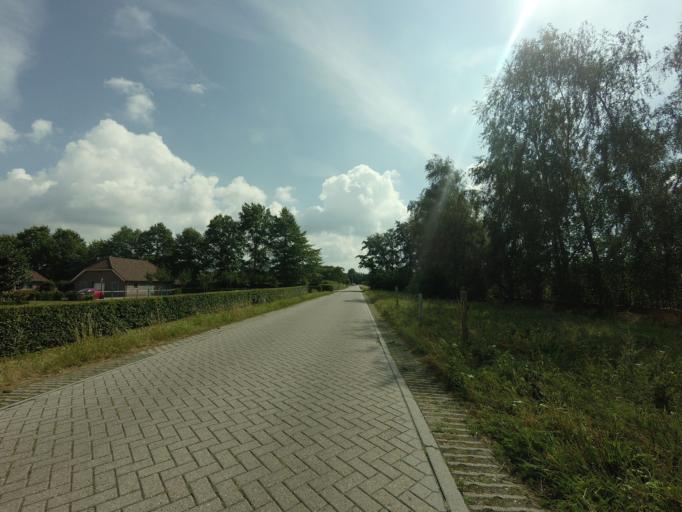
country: NL
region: Gelderland
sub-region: Gemeente Putten
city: Putten
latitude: 52.2540
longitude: 5.5605
